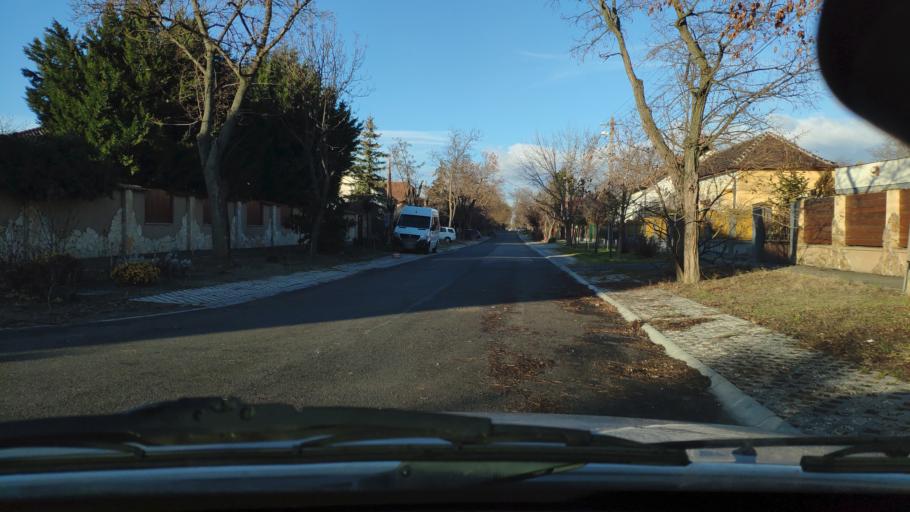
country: HU
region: Budapest
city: Budapest XXI. keruelet
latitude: 47.4164
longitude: 19.0804
